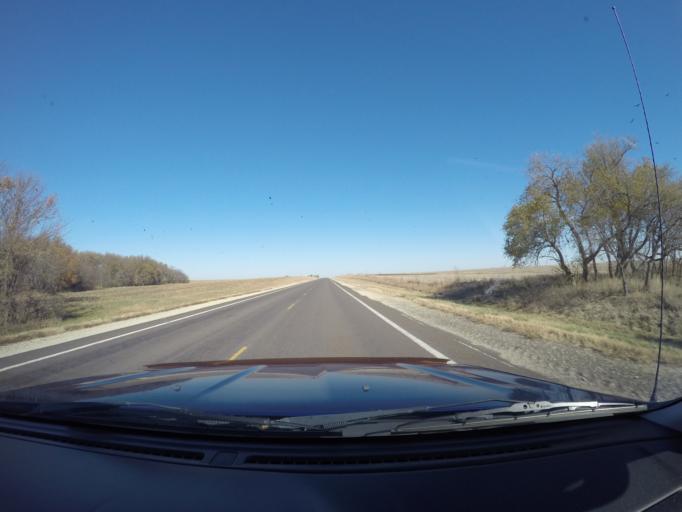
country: US
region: Kansas
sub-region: Marshall County
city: Blue Rapids
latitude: 39.6261
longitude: -96.7504
